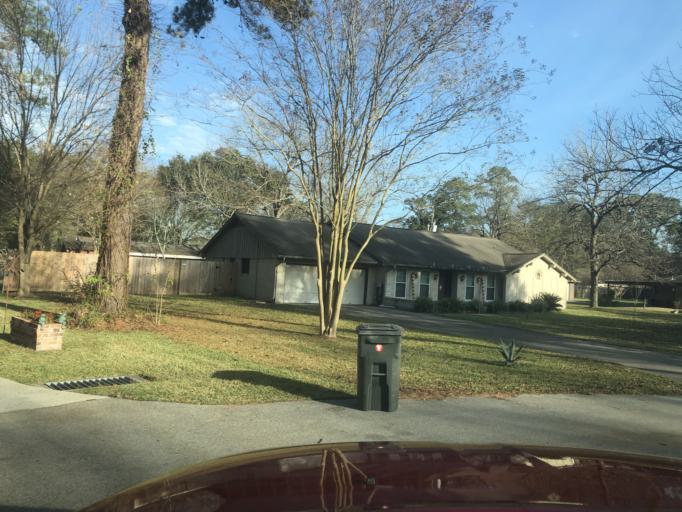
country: US
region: Texas
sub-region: Harris County
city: Spring
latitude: 30.0151
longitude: -95.4725
